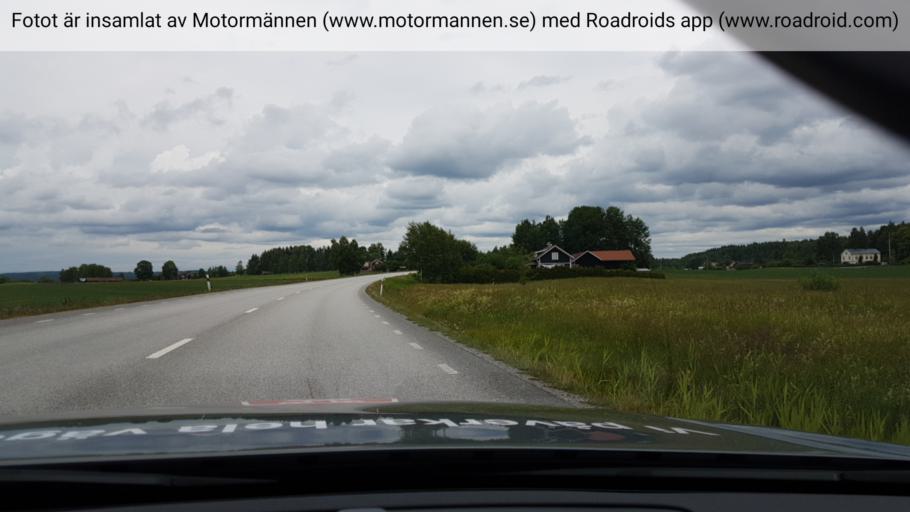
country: SE
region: OErebro
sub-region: Lindesbergs Kommun
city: Lindesberg
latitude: 59.6319
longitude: 15.2159
